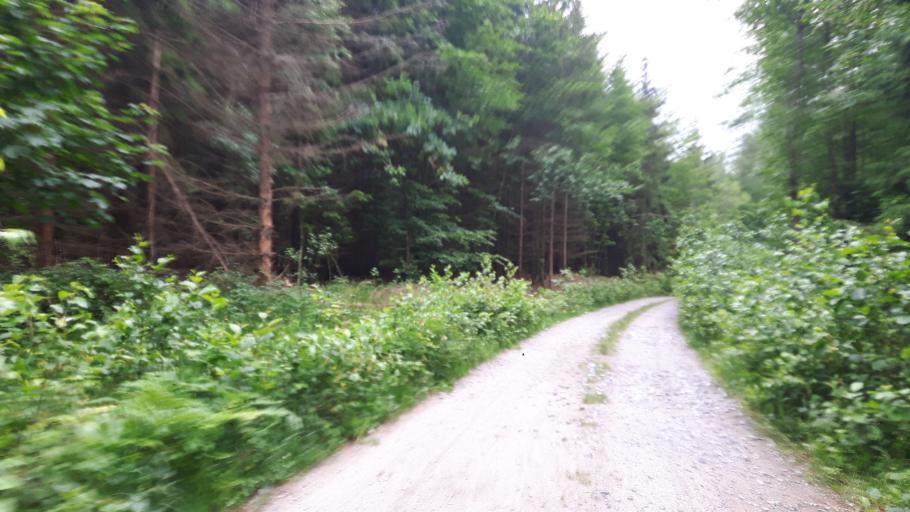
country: PL
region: Warmian-Masurian Voivodeship
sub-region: Powiat braniewski
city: Frombork
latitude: 54.3116
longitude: 19.6328
